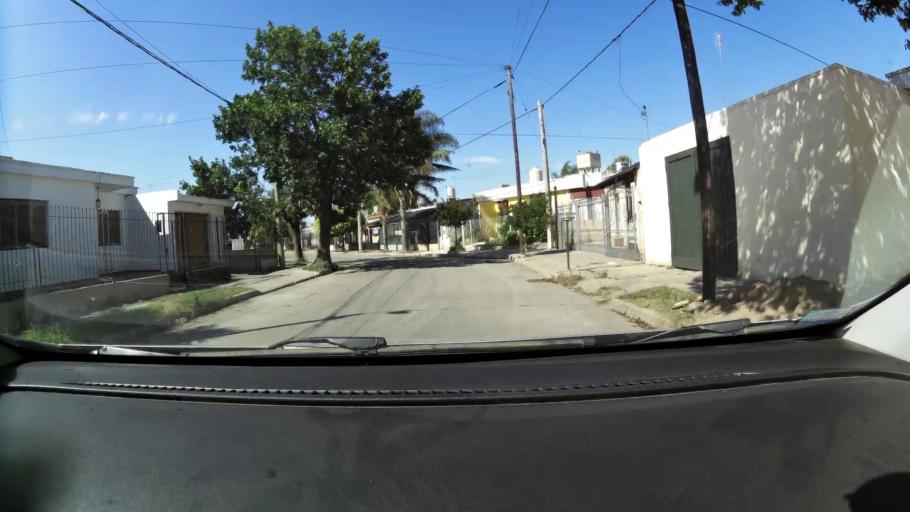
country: AR
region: Cordoba
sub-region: Departamento de Capital
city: Cordoba
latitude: -31.3626
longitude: -64.1666
